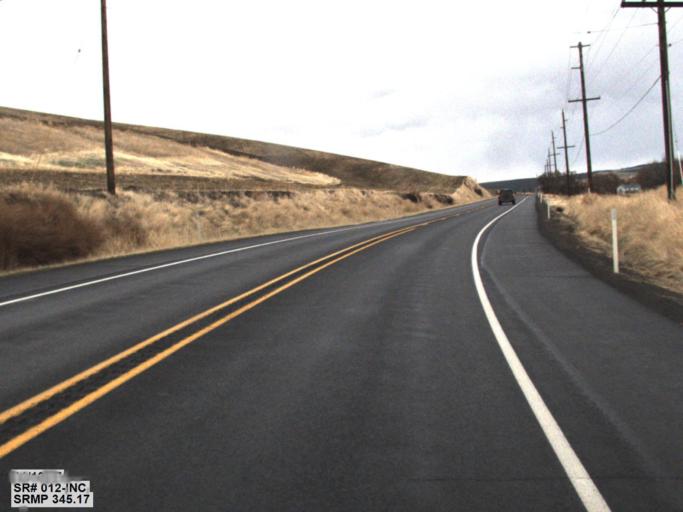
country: US
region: Washington
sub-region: Walla Walla County
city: Walla Walla East
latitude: 46.1235
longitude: -118.2051
